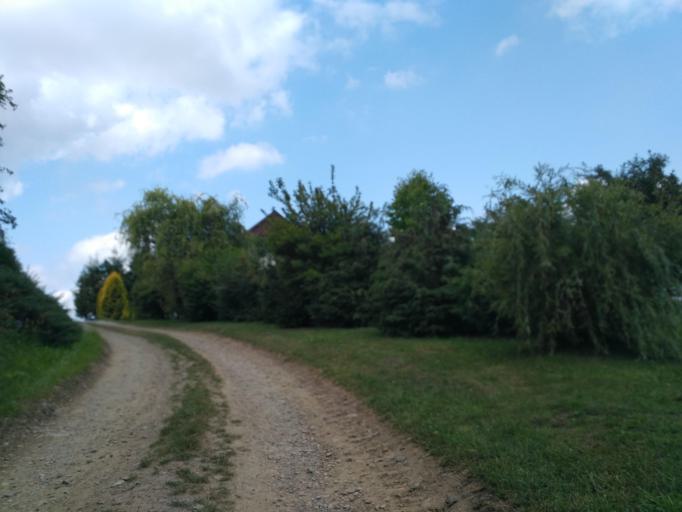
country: PL
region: Subcarpathian Voivodeship
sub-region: Powiat krosnienski
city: Iwonicz-Zdroj
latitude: 49.5952
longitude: 21.8011
